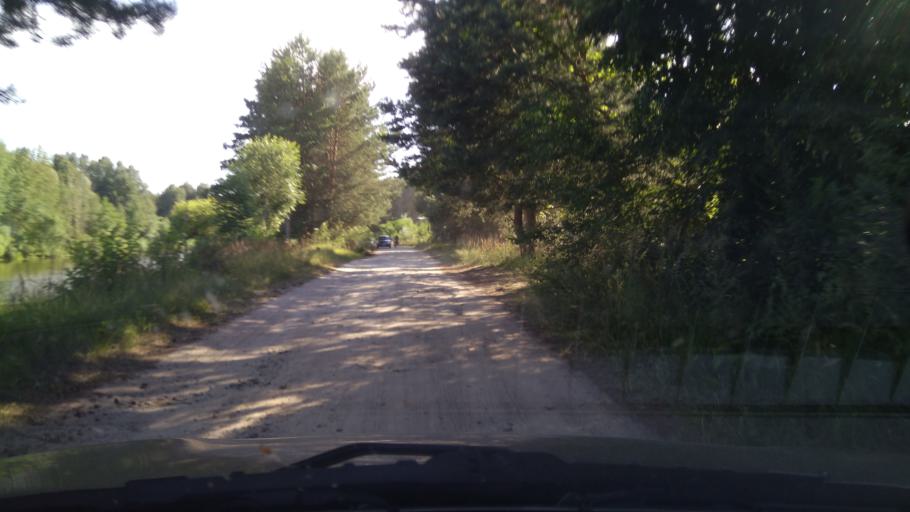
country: BY
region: Brest
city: Byelaazyorsk
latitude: 52.4456
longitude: 25.1768
